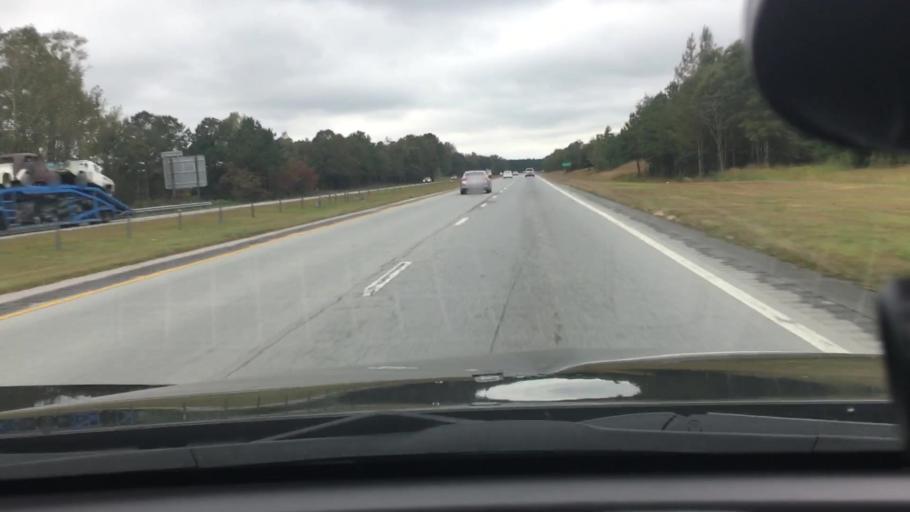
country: US
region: North Carolina
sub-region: Pitt County
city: Farmville
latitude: 35.6193
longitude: -77.6898
